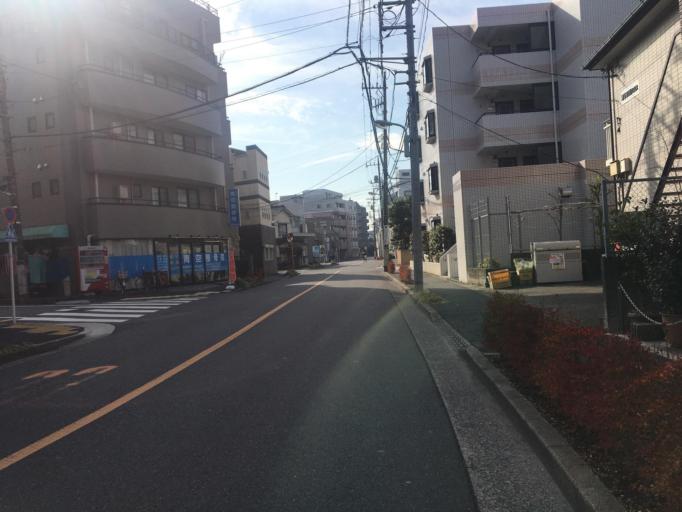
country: JP
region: Tokyo
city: Urayasu
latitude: 35.7102
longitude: 139.8412
